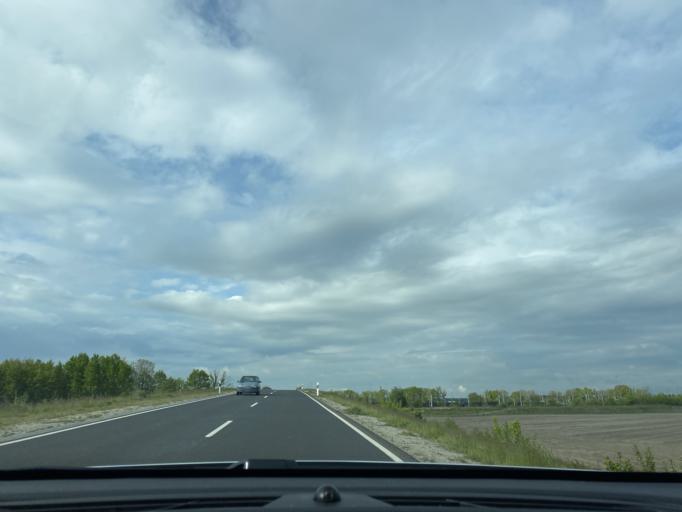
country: DE
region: Saxony
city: Horka
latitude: 51.3067
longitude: 14.9258
